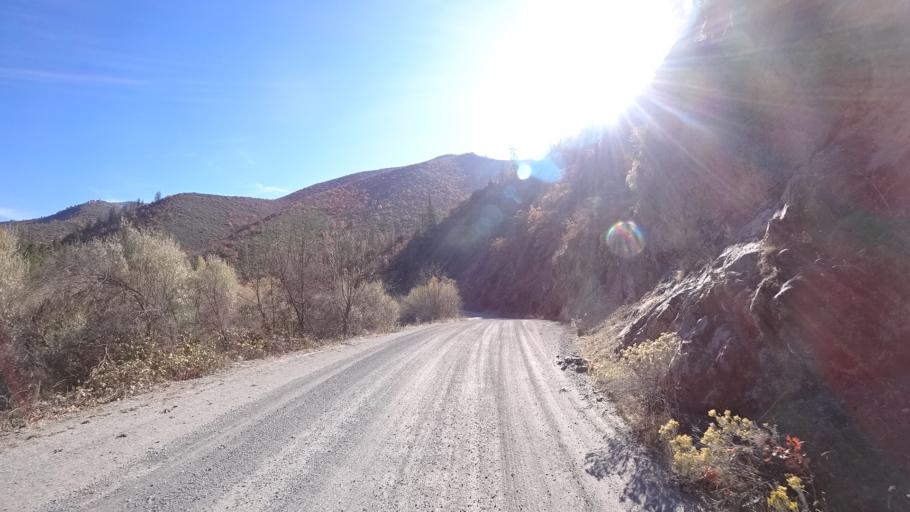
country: US
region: California
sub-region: Siskiyou County
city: Yreka
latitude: 41.8264
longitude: -122.6610
